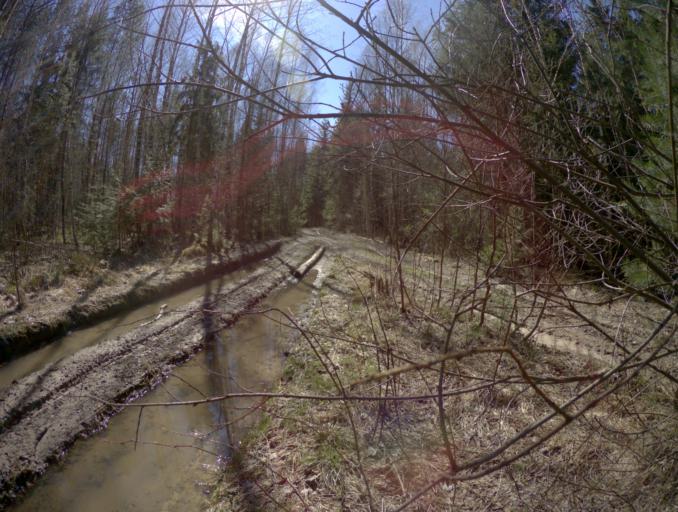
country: RU
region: Vladimir
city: Ivanishchi
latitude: 55.8322
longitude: 40.4320
